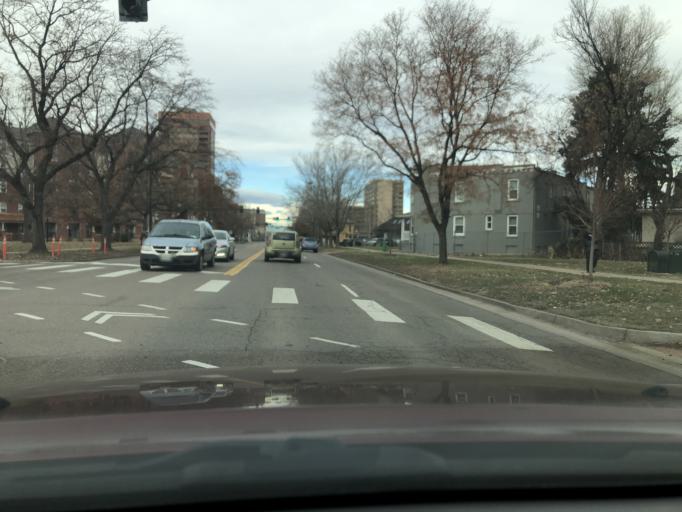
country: US
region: Colorado
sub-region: Denver County
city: Denver
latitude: 39.7462
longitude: -104.9765
